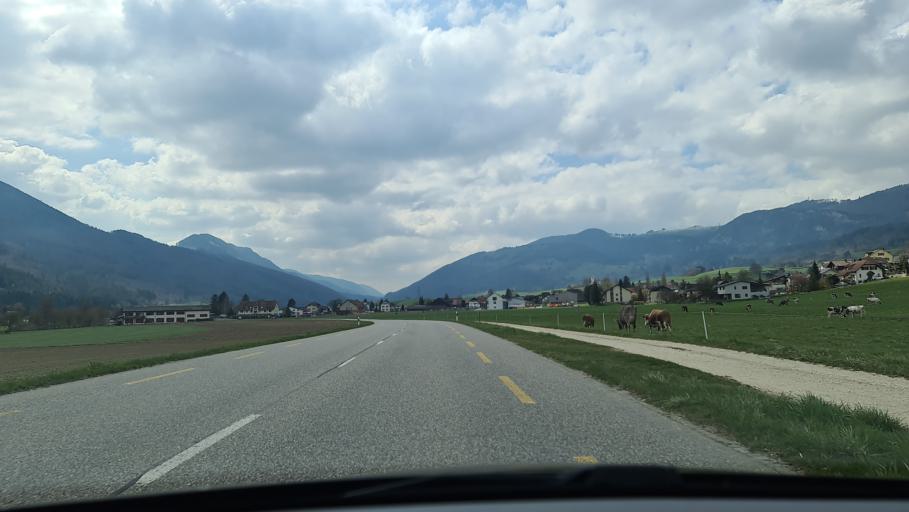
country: CH
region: Solothurn
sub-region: Bezirk Thal
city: Matzendorf
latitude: 47.3070
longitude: 7.6392
